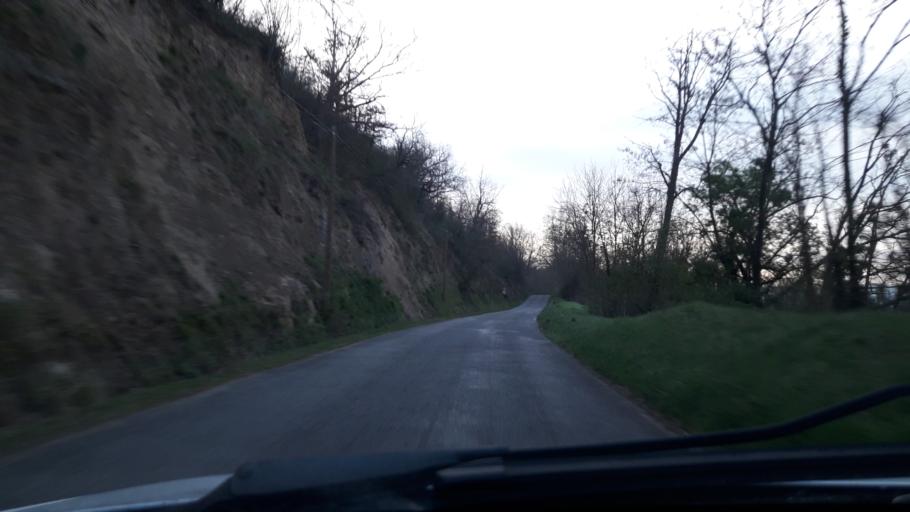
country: FR
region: Midi-Pyrenees
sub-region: Departement de la Haute-Garonne
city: Montesquieu-Volvestre
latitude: 43.1987
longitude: 1.2447
